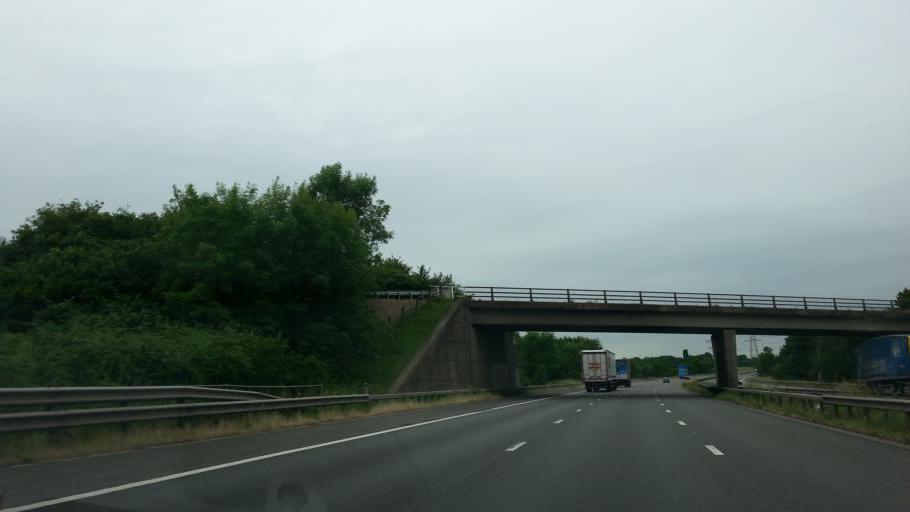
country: GB
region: England
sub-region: Leicestershire
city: Hinckley
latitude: 52.5277
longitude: -1.3293
